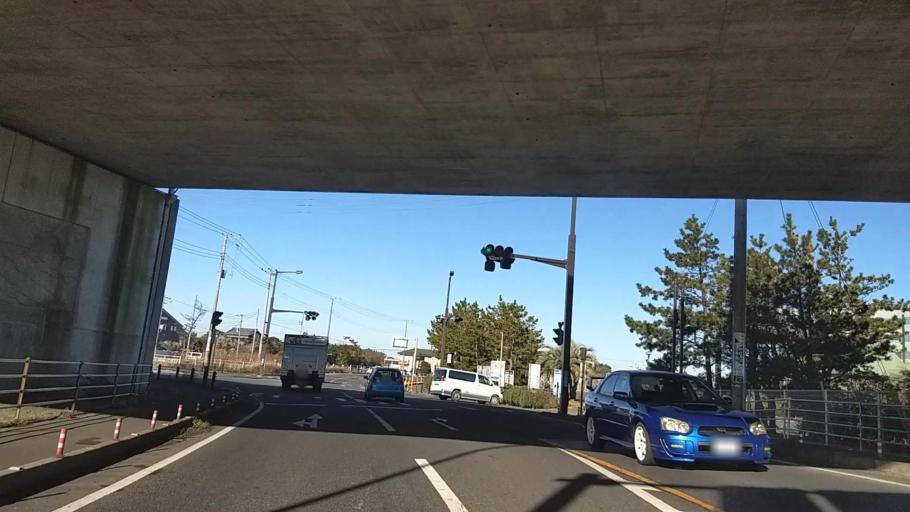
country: JP
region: Chiba
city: Togane
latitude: 35.5000
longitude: 140.4286
